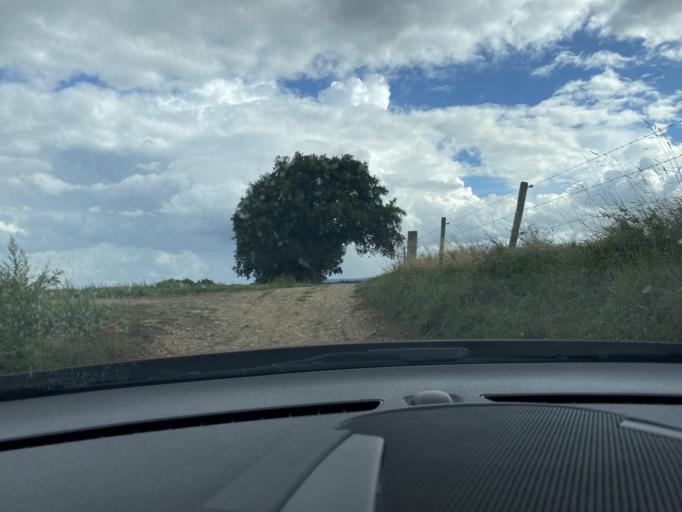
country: NL
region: Limburg
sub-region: Gemeente Simpelveld
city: Simpelveld
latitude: 50.8342
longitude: 5.9651
